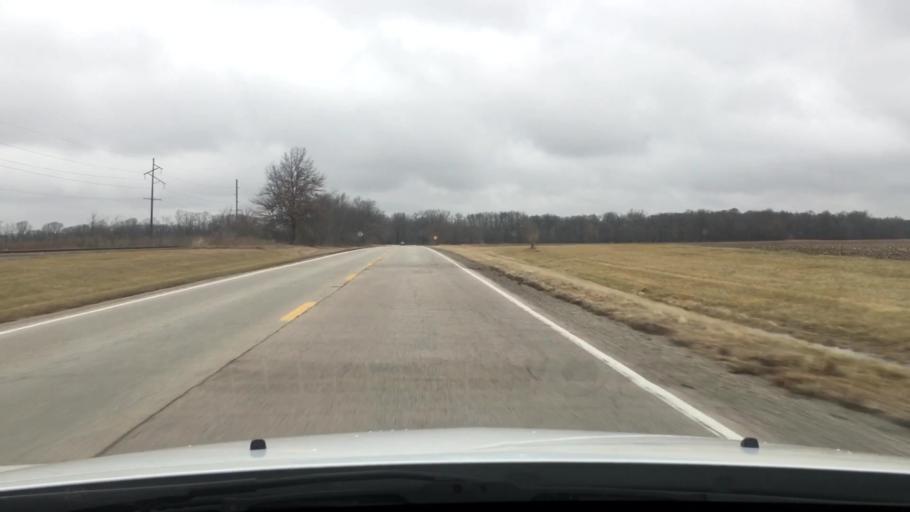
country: US
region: Illinois
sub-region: Iroquois County
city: Sheldon
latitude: 40.8096
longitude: -87.5756
